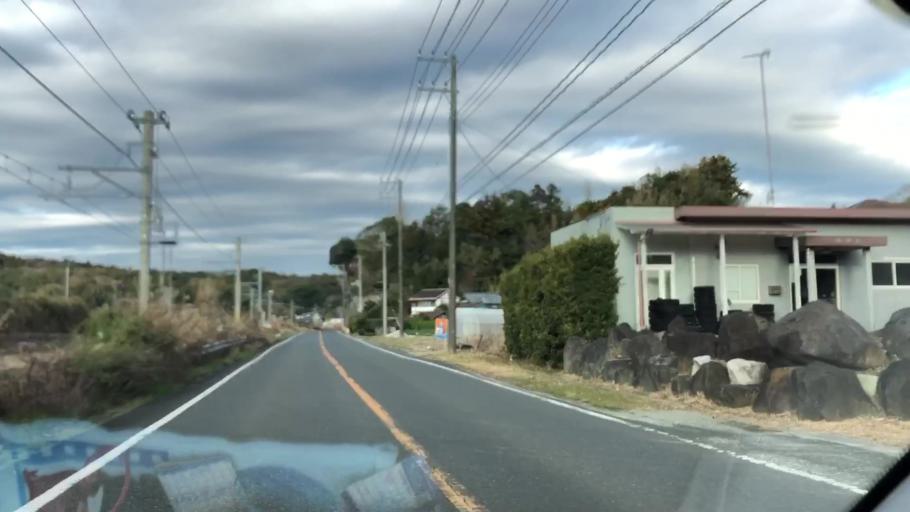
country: JP
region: Chiba
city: Tateyama
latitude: 34.9908
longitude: 139.9240
